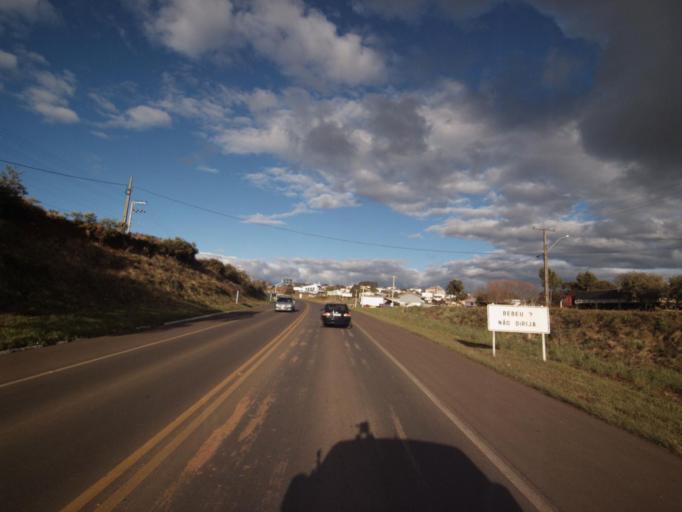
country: BR
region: Santa Catarina
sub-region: Campos Novos
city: Campos Novos
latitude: -27.3875
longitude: -51.2328
